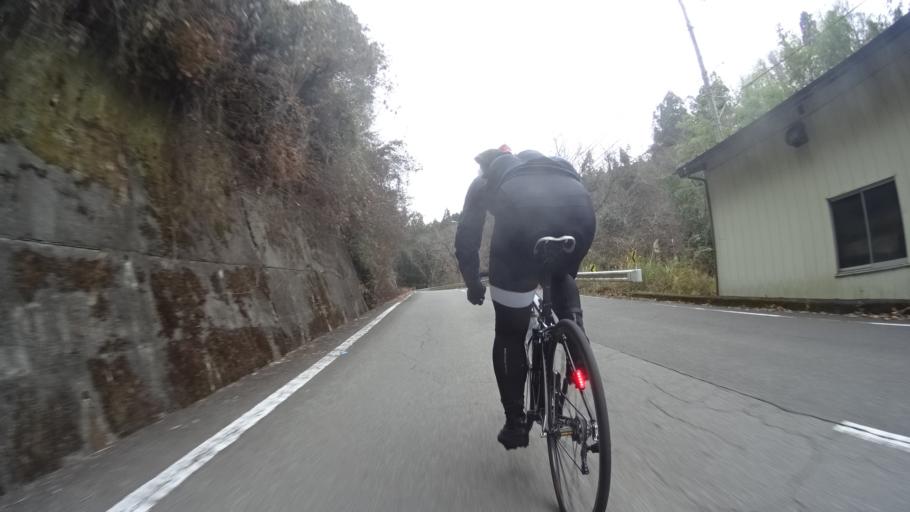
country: JP
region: Yamanashi
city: Uenohara
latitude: 35.6384
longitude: 139.0707
